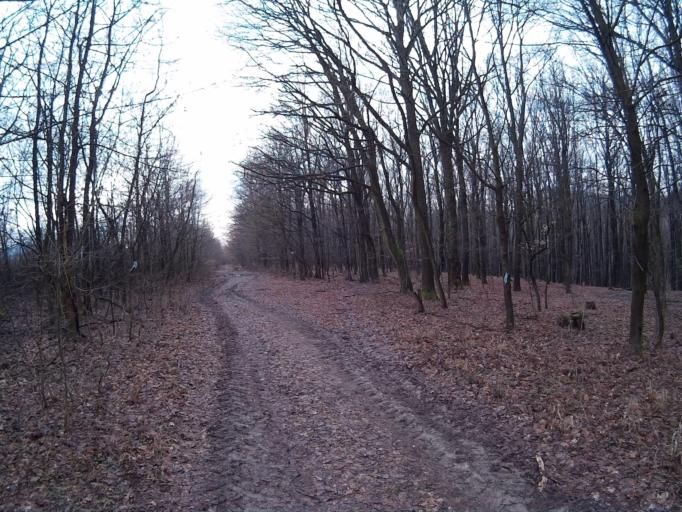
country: HU
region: Borsod-Abauj-Zemplen
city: Satoraljaujhely
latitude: 48.4145
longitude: 21.5980
